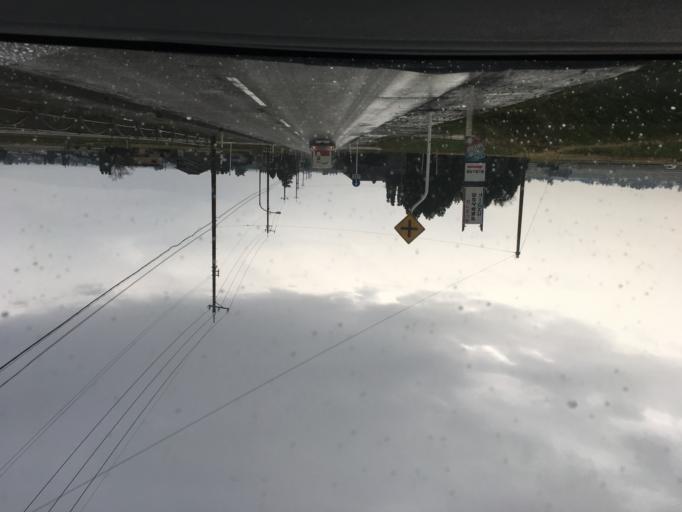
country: JP
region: Toyama
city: Nanto-shi
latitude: 36.5551
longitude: 136.9555
